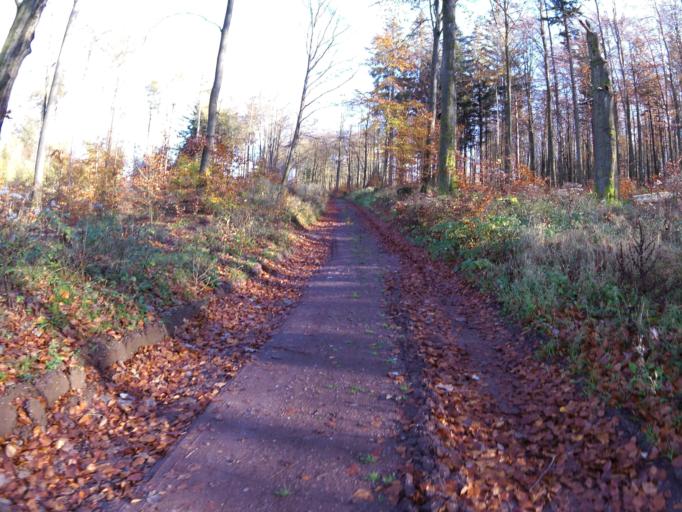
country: DE
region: Thuringia
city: Ruhla
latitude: 50.9072
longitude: 10.3361
